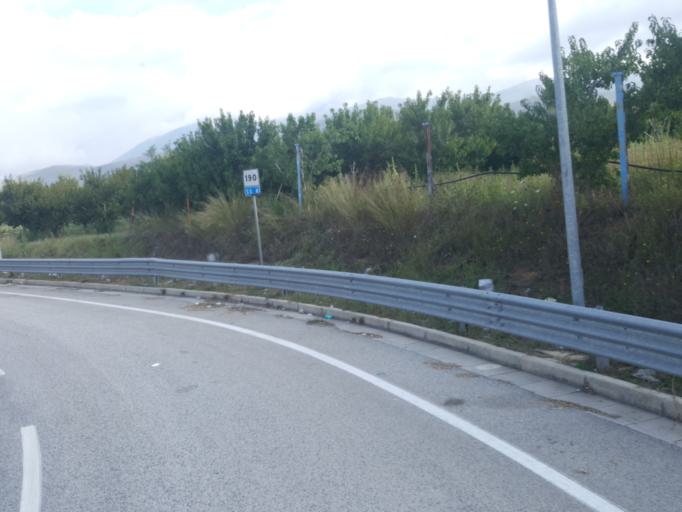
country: IT
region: Campania
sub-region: Provincia di Caserta
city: Pignataro Maggiore
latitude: 41.1802
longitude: 14.1576
